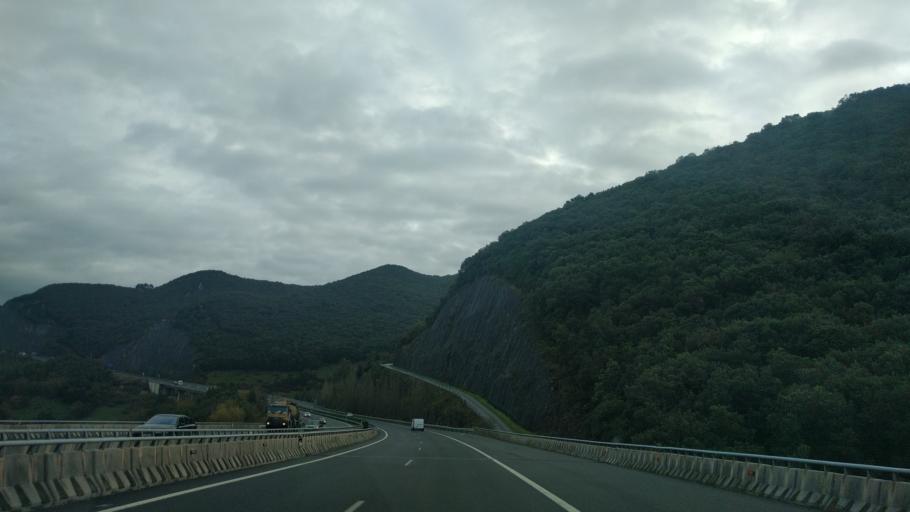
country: ES
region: Cantabria
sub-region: Provincia de Cantabria
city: Liendo
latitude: 43.3805
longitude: -3.3726
